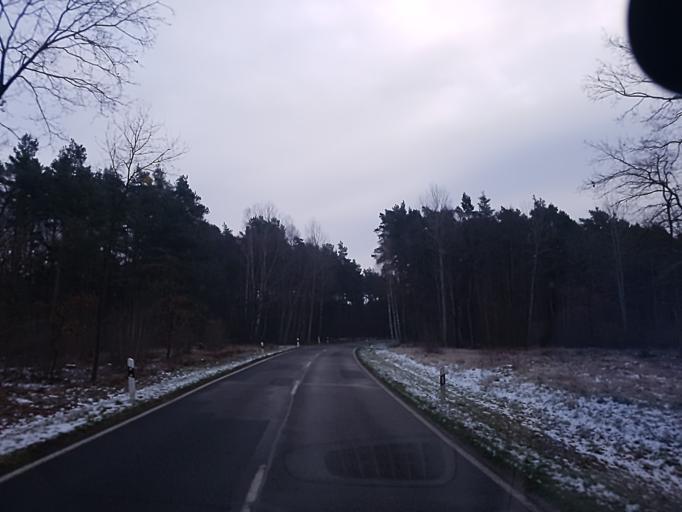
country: DE
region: Brandenburg
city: Crinitz
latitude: 51.7424
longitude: 13.8349
